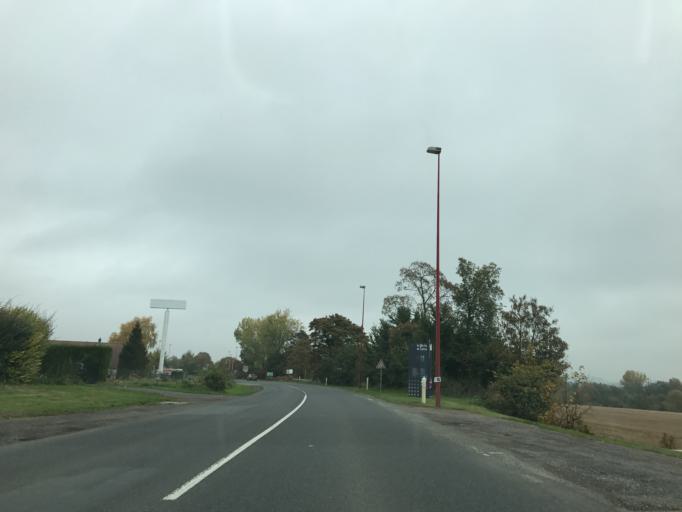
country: FR
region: Picardie
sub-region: Departement de la Somme
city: Peronne
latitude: 49.9057
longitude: 2.9300
